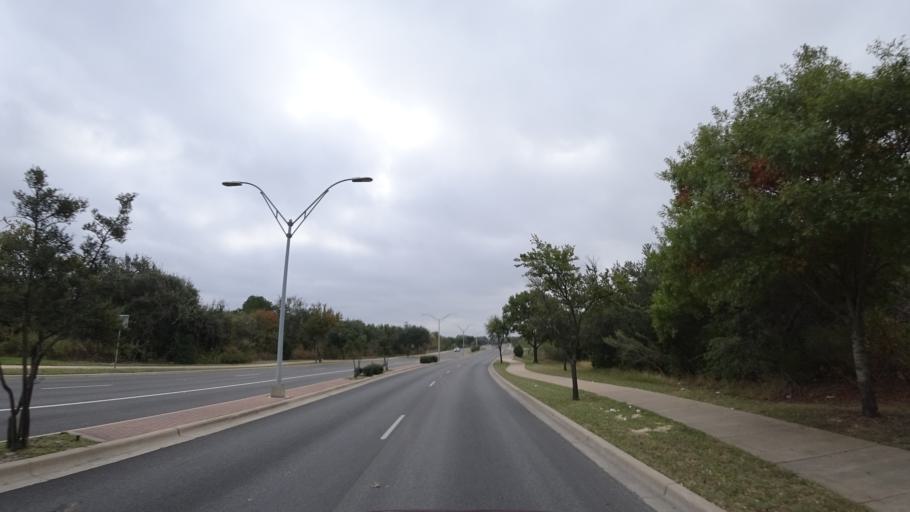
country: US
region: Texas
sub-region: Williamson County
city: Cedar Park
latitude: 30.5135
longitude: -97.8507
